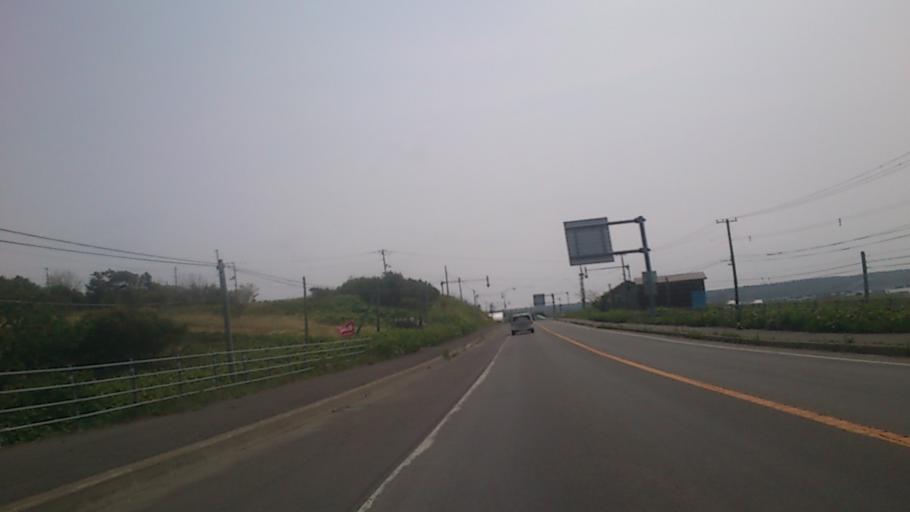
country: JP
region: Hokkaido
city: Nemuro
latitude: 43.2818
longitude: 145.5072
